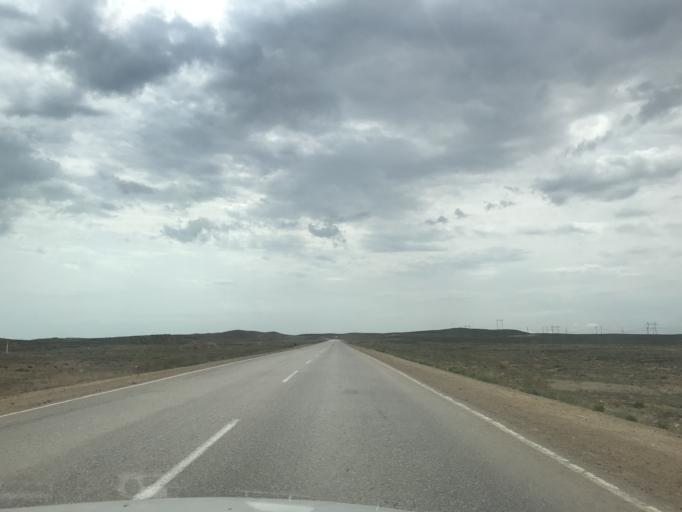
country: KZ
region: Zhambyl
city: Mynaral
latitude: 45.5200
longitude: 73.4893
